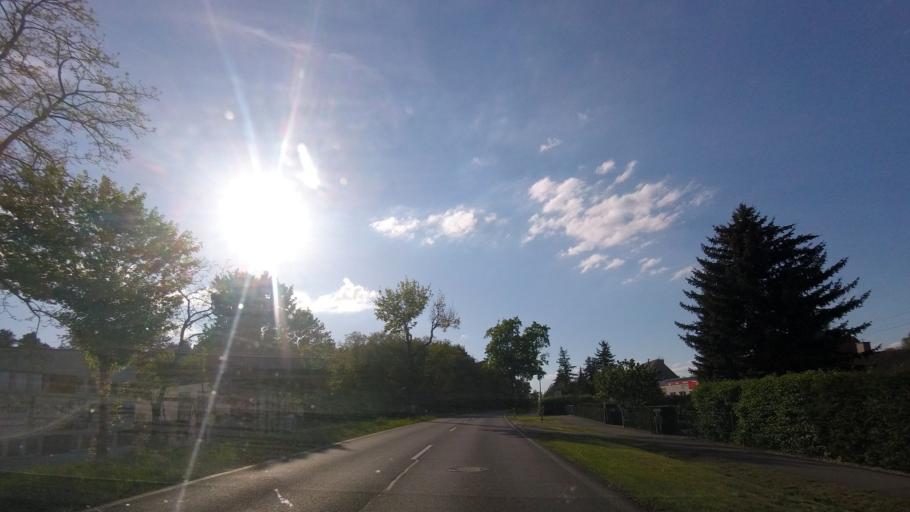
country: DE
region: Brandenburg
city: Lubbenau
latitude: 51.8652
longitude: 13.9243
